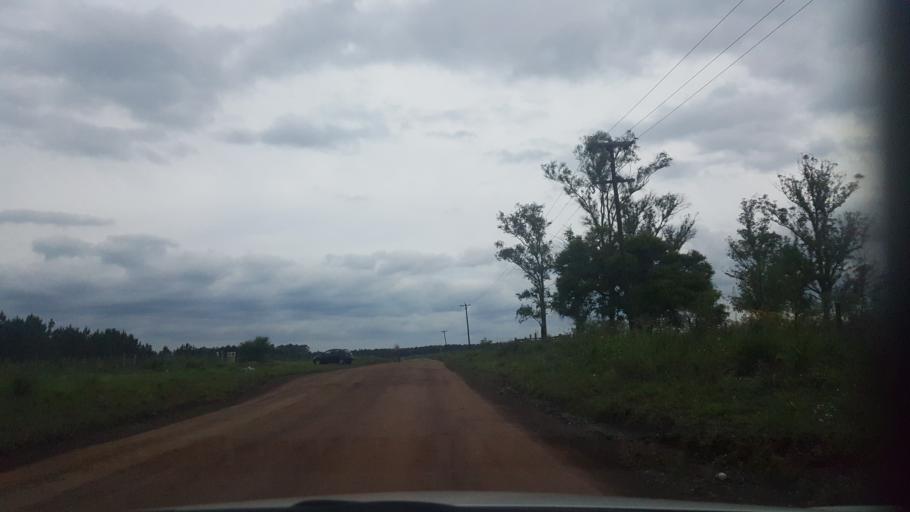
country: AR
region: Misiones
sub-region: Departamento de Candelaria
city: Candelaria
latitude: -27.4999
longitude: -55.7372
